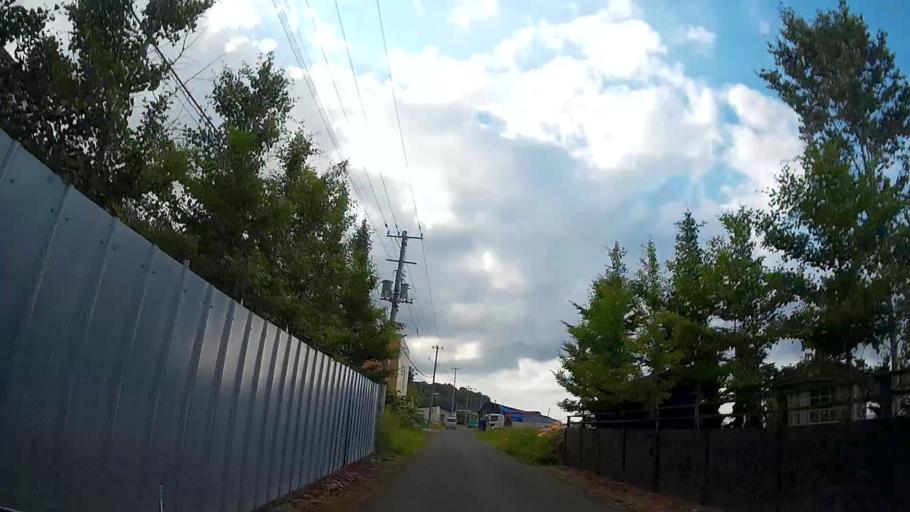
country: JP
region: Hokkaido
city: Nanae
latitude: 42.1153
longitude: 140.5438
